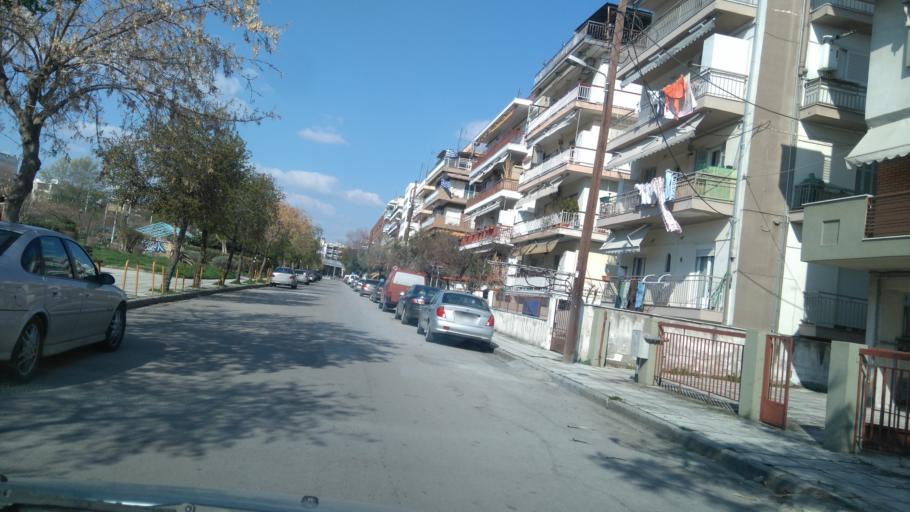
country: GR
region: Central Macedonia
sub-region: Nomos Thessalonikis
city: Ampelokipoi
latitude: 40.6597
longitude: 22.9279
